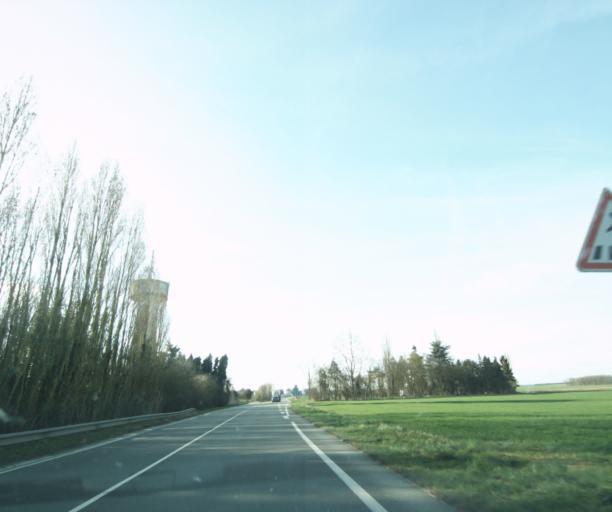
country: FR
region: Ile-de-France
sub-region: Departement des Yvelines
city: Ablis
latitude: 48.4645
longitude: 1.8793
